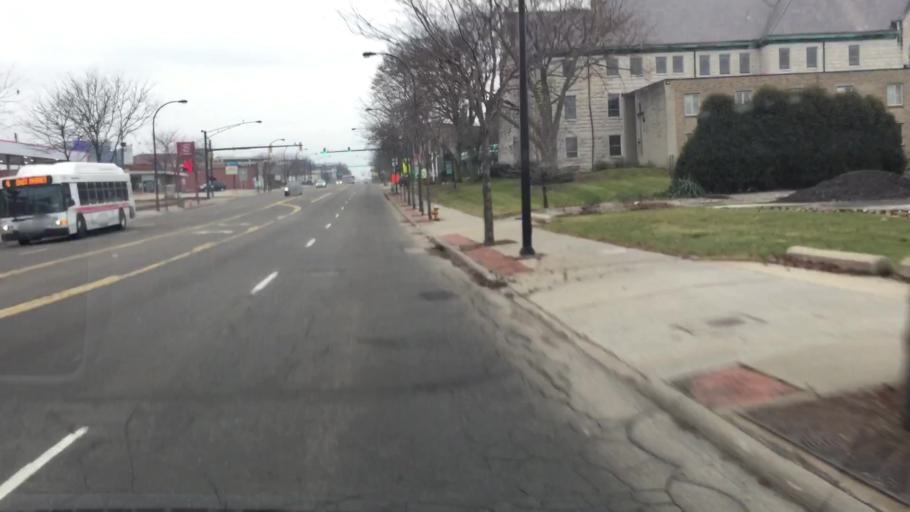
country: US
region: Ohio
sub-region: Summit County
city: Akron
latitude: 41.0821
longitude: -81.5093
